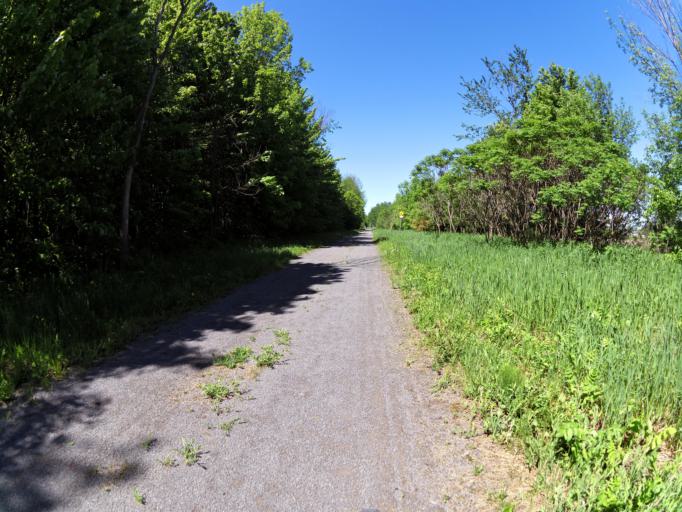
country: CA
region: Ontario
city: Clarence-Rockland
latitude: 45.4244
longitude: -75.3321
